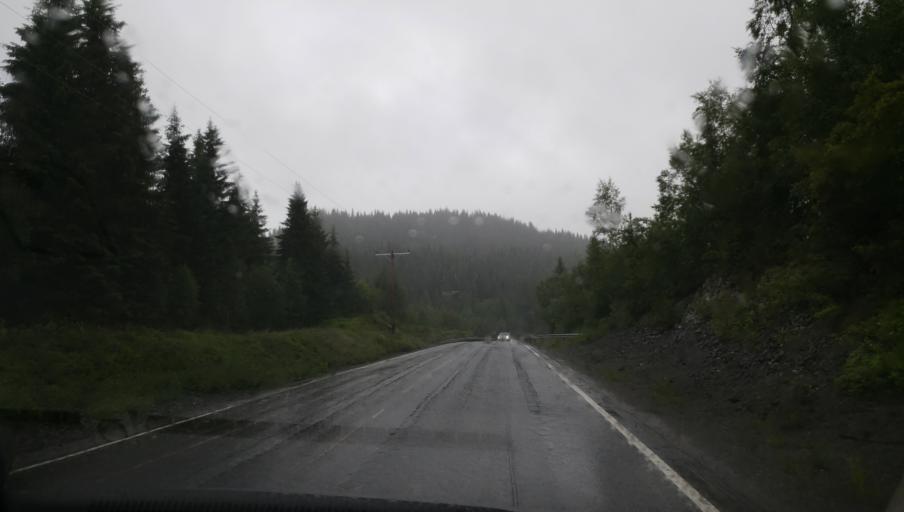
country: NO
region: Sor-Trondelag
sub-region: Selbu
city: Mebonden
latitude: 63.3500
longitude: 11.0779
